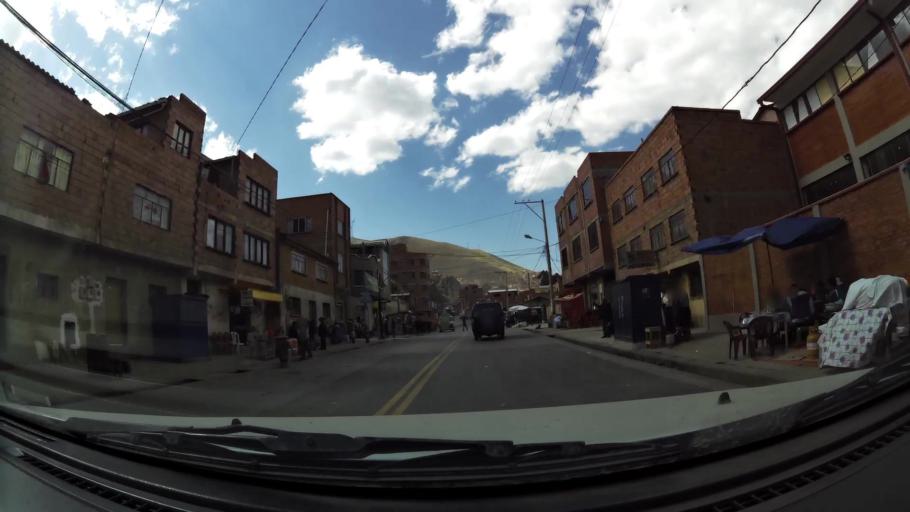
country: BO
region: La Paz
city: La Paz
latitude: -16.4596
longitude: -68.1028
